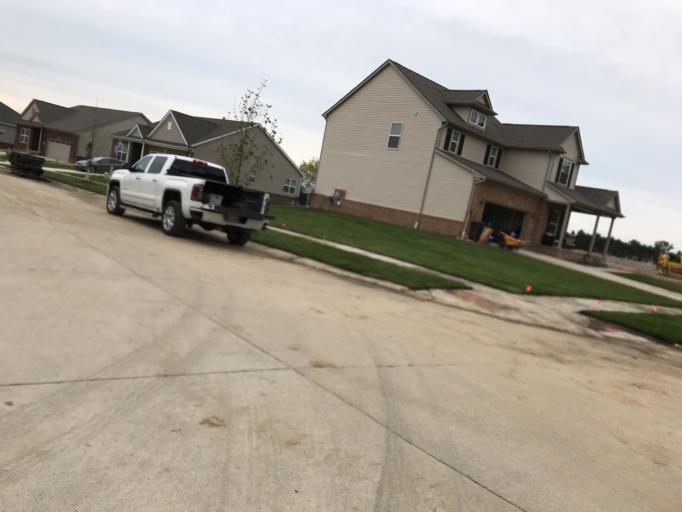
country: US
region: Michigan
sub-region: Oakland County
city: South Lyon
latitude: 42.4705
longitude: -83.6434
